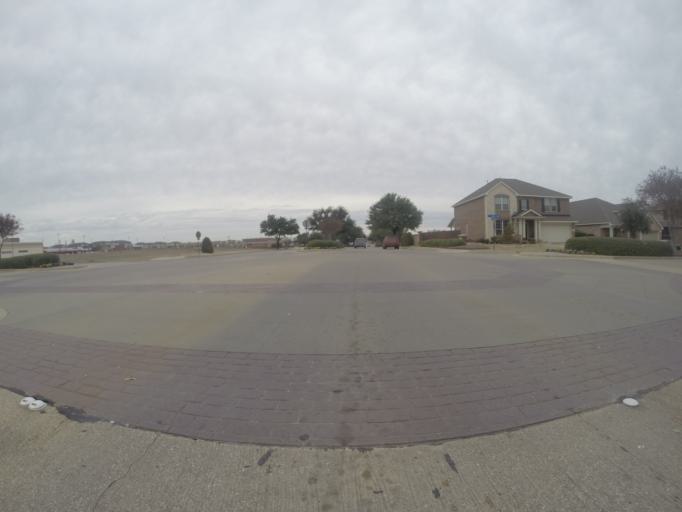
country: US
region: Texas
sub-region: Collin County
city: Saint Paul
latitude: 33.0410
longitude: -96.5685
